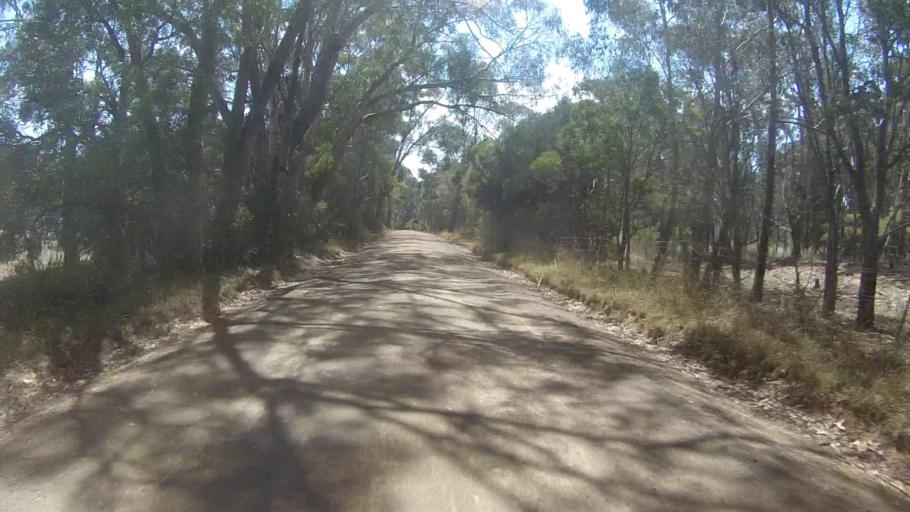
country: AU
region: Tasmania
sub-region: Sorell
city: Sorell
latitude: -42.8562
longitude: 147.8339
